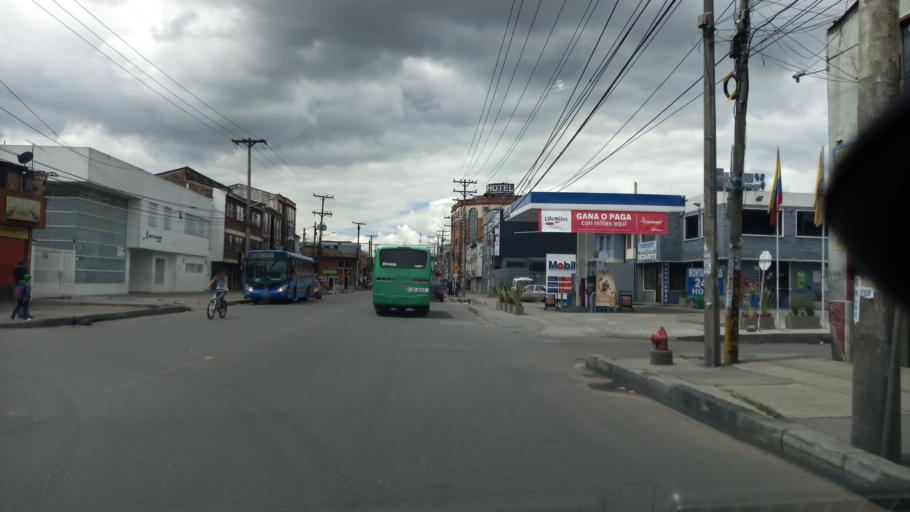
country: CO
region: Cundinamarca
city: Funza
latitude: 4.6697
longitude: -74.1434
